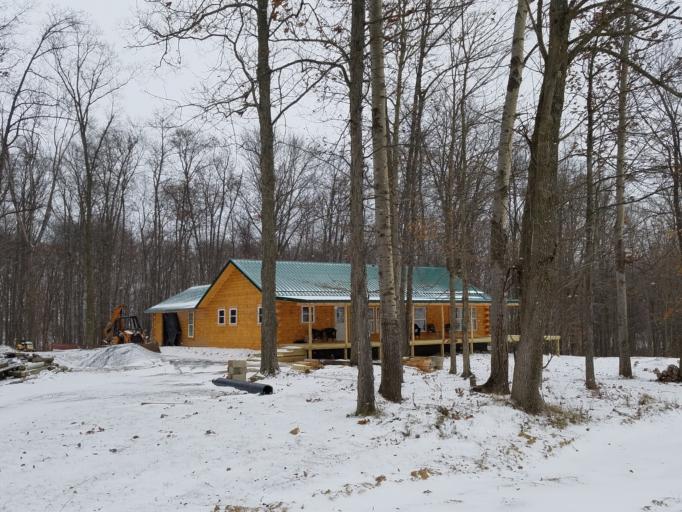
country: US
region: Ohio
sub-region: Morrow County
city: Mount Gilead
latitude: 40.5859
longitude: -82.7000
